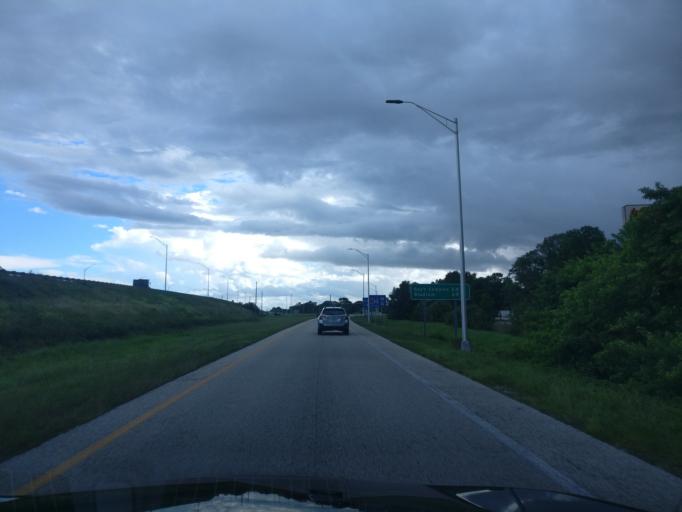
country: US
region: Florida
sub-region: Brevard County
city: South Patrick Shores
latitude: 28.2328
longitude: -80.7197
